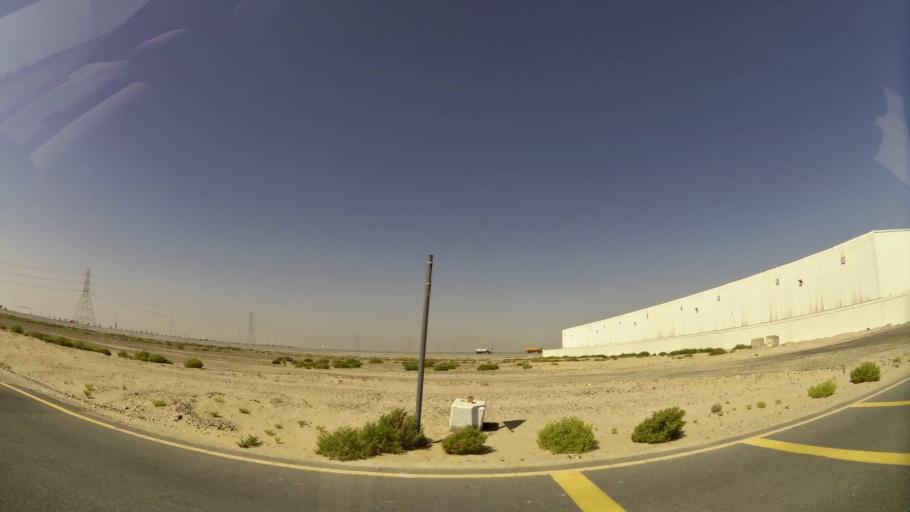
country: AE
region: Dubai
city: Dubai
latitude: 24.8986
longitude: 55.0553
